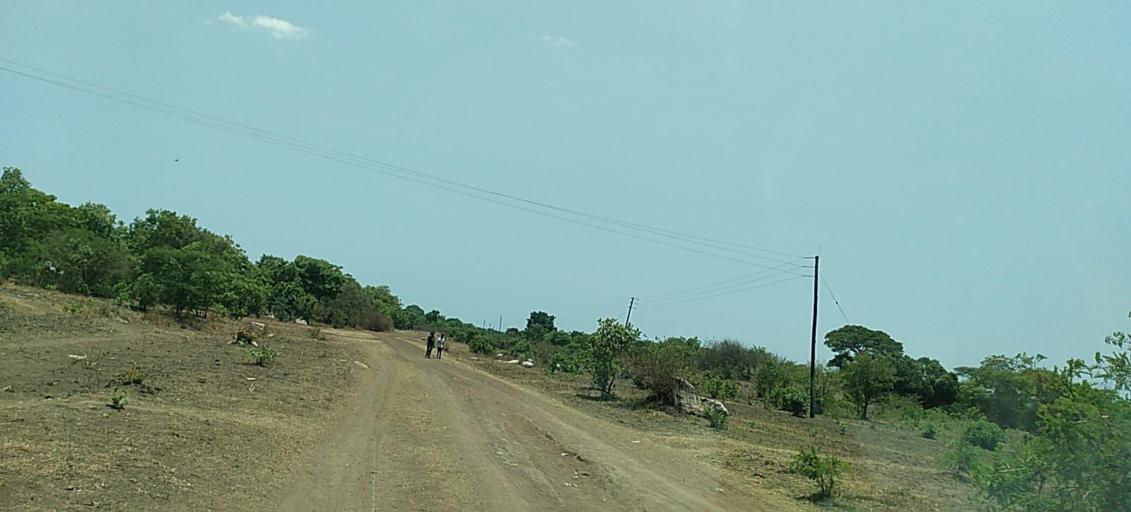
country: ZM
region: Copperbelt
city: Mpongwe
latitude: -13.8320
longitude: 27.8383
